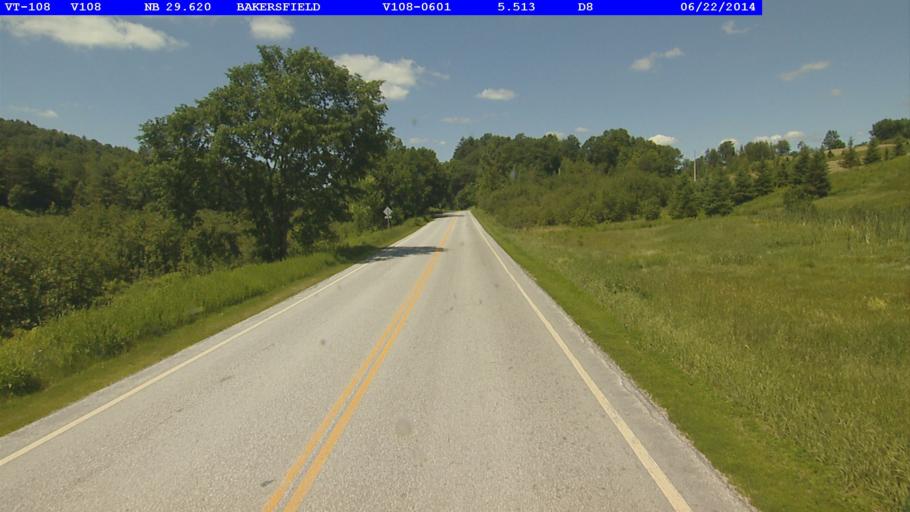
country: US
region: Vermont
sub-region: Franklin County
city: Enosburg Falls
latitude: 44.8062
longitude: -72.7875
